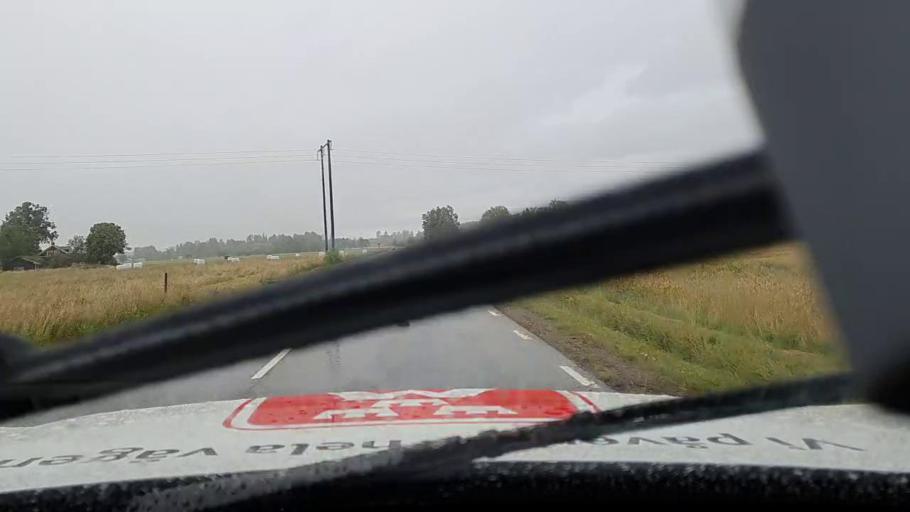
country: SE
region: Vaestra Goetaland
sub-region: Toreboda Kommun
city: Toereboda
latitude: 58.6933
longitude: 14.1302
